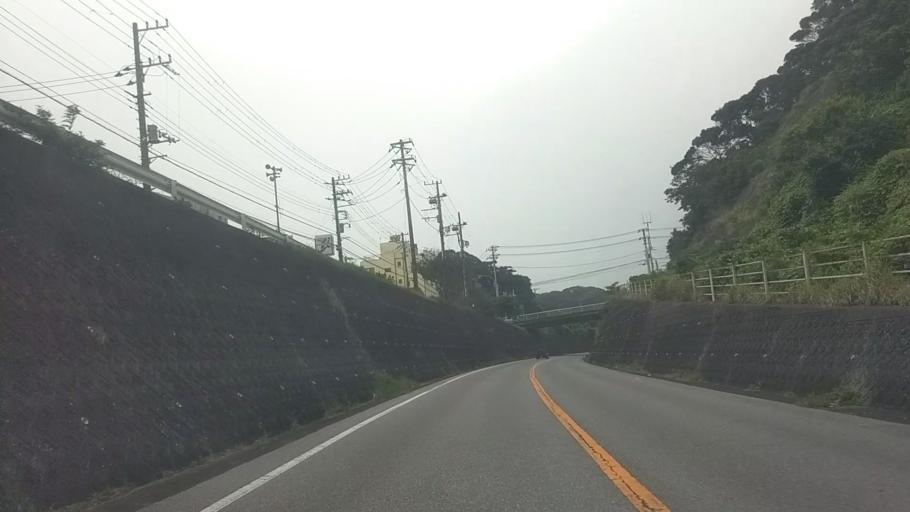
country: JP
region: Chiba
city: Katsuura
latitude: 35.1593
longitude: 140.3169
